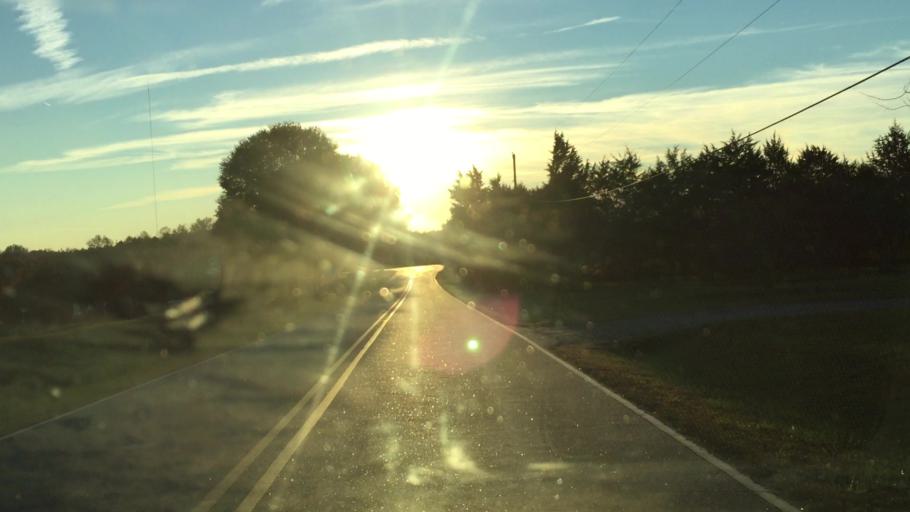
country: US
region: North Carolina
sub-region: Iredell County
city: Mooresville
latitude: 35.5470
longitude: -80.7729
